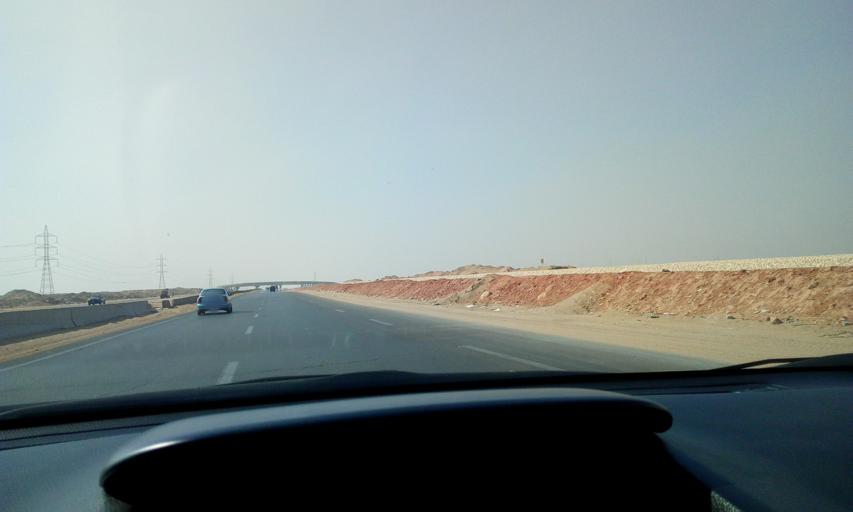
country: EG
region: Al Jizah
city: Madinat Sittah Uktubar
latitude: 29.9184
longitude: 31.0929
